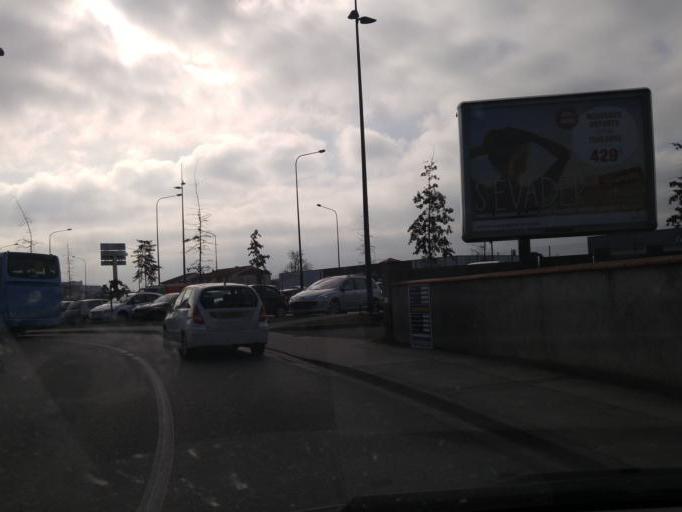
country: FR
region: Midi-Pyrenees
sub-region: Departement de la Haute-Garonne
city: Blagnac
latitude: 43.6409
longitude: 1.3757
